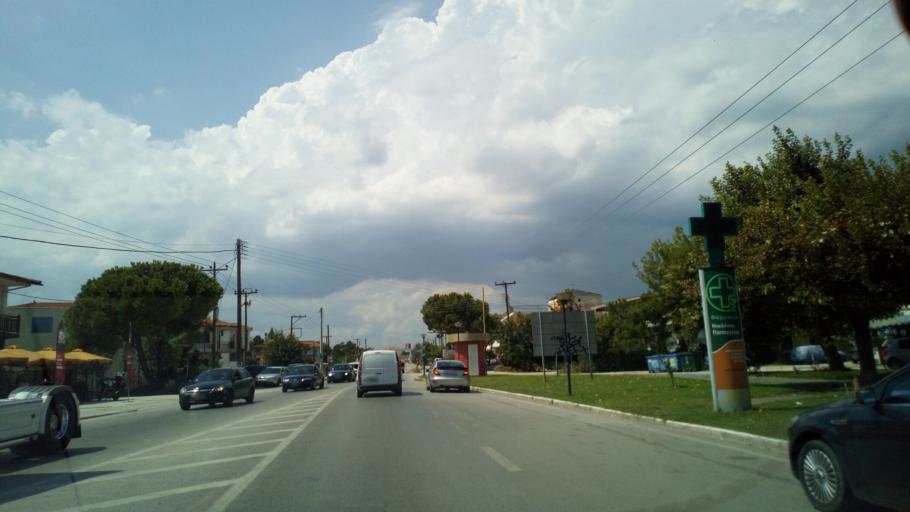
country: GR
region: Central Macedonia
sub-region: Nomos Chalkidikis
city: Nikiti
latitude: 40.2239
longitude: 23.6671
